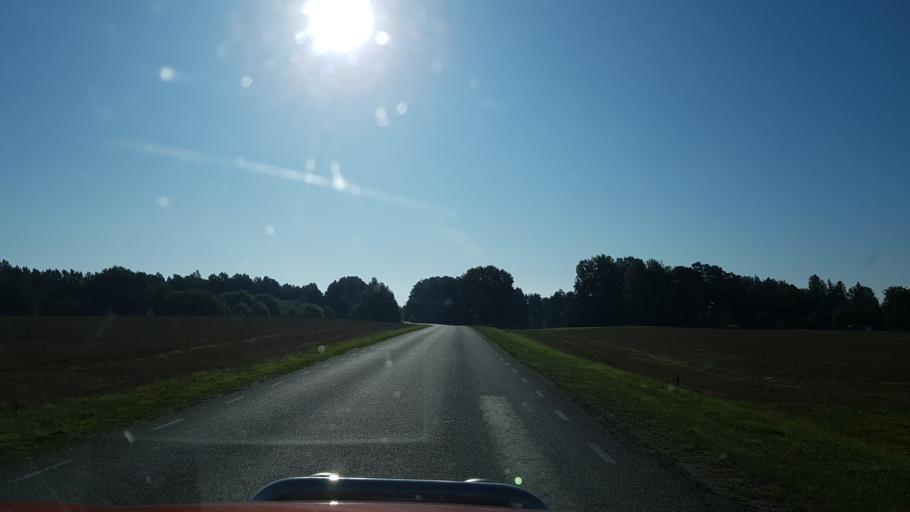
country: EE
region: Jogevamaa
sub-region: Tabivere vald
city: Tabivere
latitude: 58.6809
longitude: 26.6185
